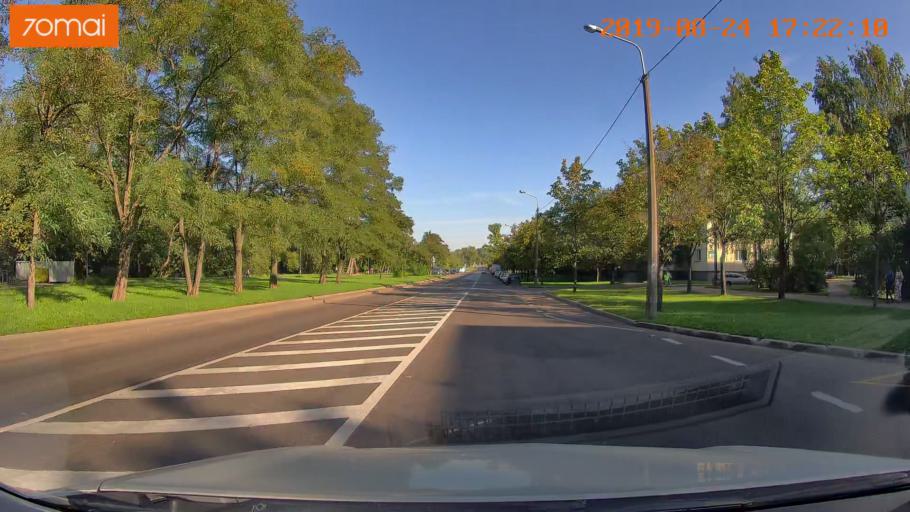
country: BY
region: Minsk
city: Hatava
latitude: 53.8471
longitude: 27.6415
